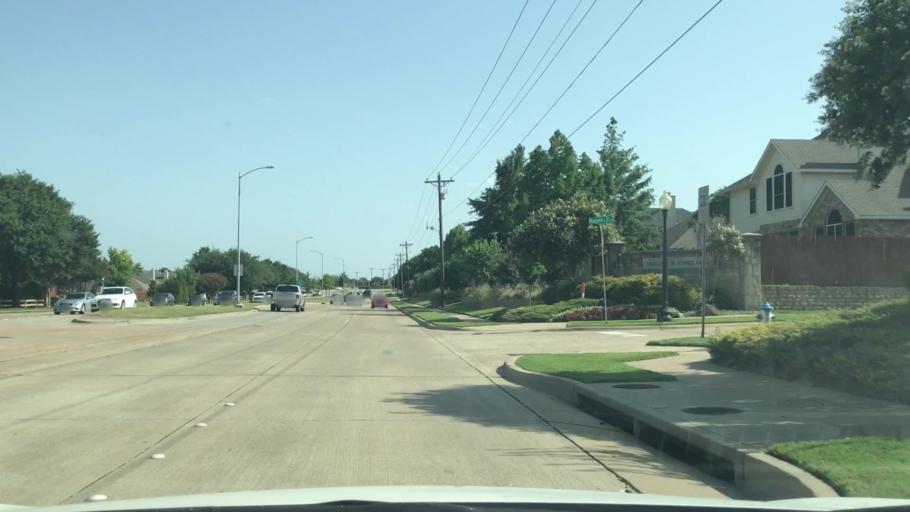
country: US
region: Texas
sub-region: Collin County
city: Allen
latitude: 33.1076
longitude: -96.7509
